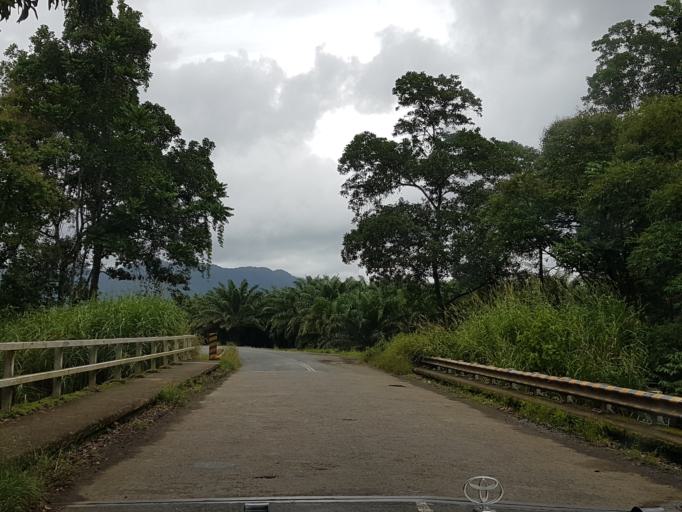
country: PG
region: Milne Bay
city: Alotau
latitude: -10.3228
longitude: 150.2789
